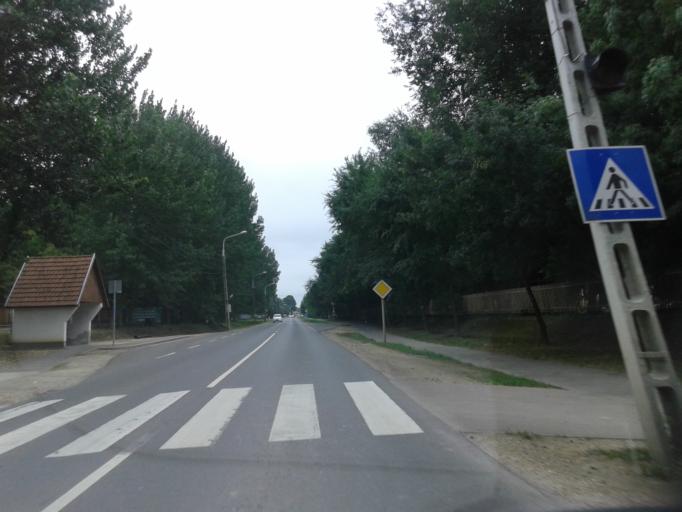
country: HU
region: Bacs-Kiskun
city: Solt
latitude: 46.8004
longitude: 19.0206
